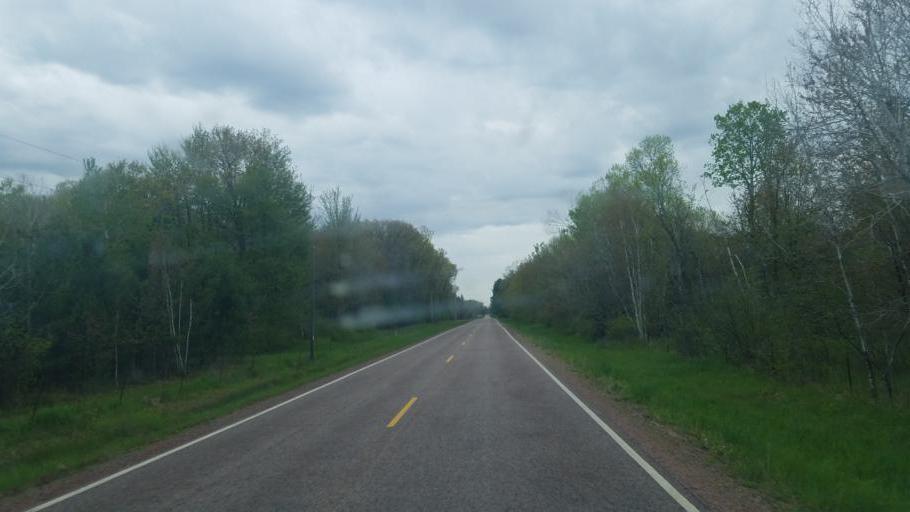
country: US
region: Wisconsin
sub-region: Wood County
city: Marshfield
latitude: 44.4577
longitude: -90.2799
